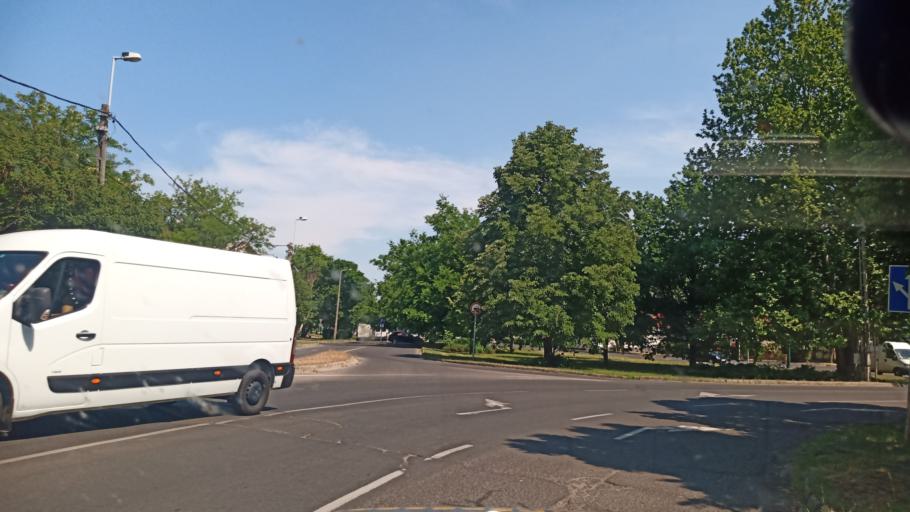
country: HU
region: Bekes
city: Oroshaza
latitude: 46.5572
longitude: 20.6603
